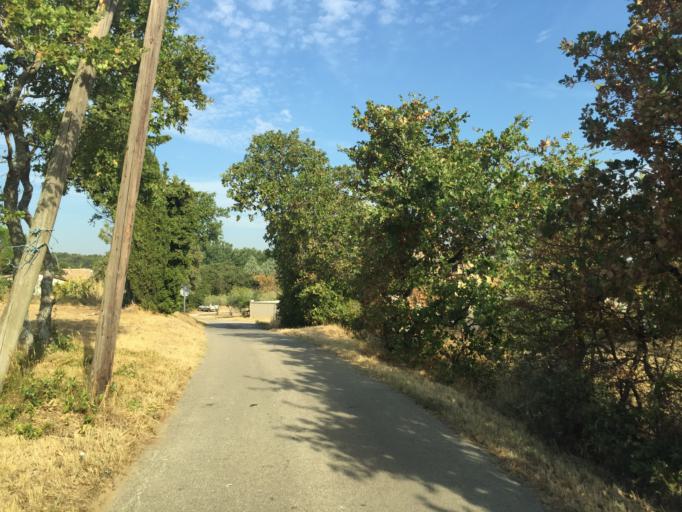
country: FR
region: Provence-Alpes-Cote d'Azur
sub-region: Departement du Vaucluse
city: Courthezon
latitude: 44.0784
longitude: 4.8667
